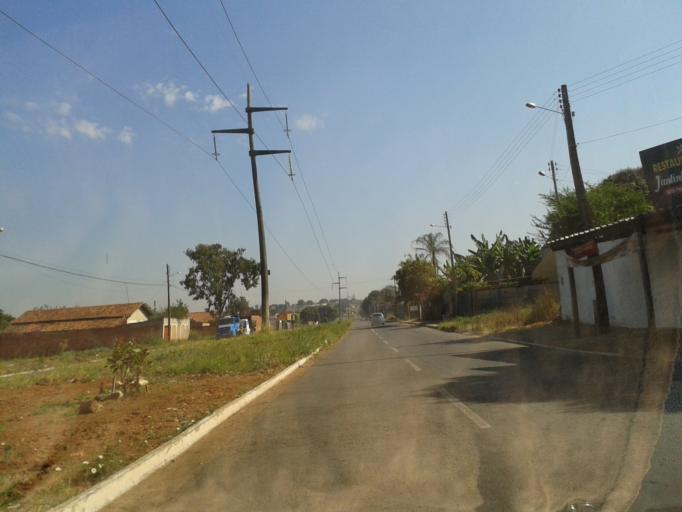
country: BR
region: Goias
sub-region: Aparecida De Goiania
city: Aparecida de Goiania
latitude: -16.7601
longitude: -49.3085
